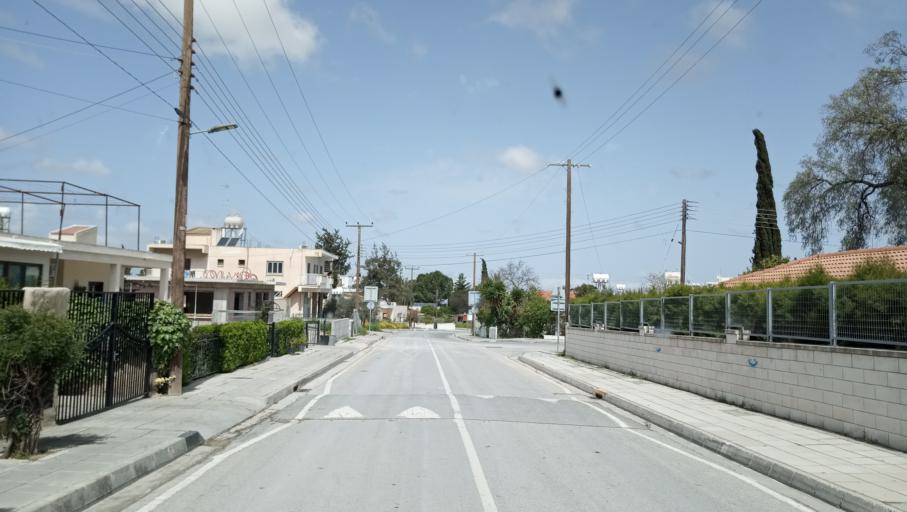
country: CY
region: Lefkosia
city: Dali
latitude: 35.0164
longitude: 33.4196
